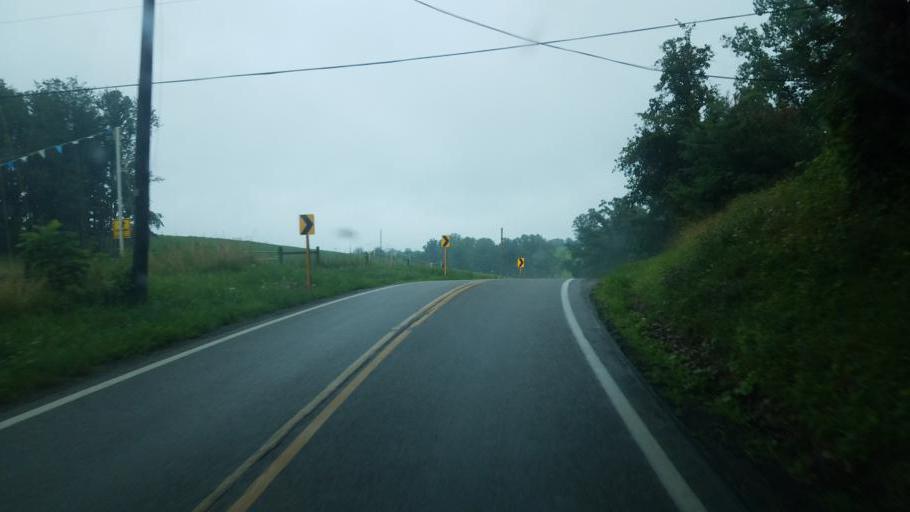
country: US
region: Ohio
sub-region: Tuscarawas County
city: Rockford
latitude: 40.4480
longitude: -81.1777
